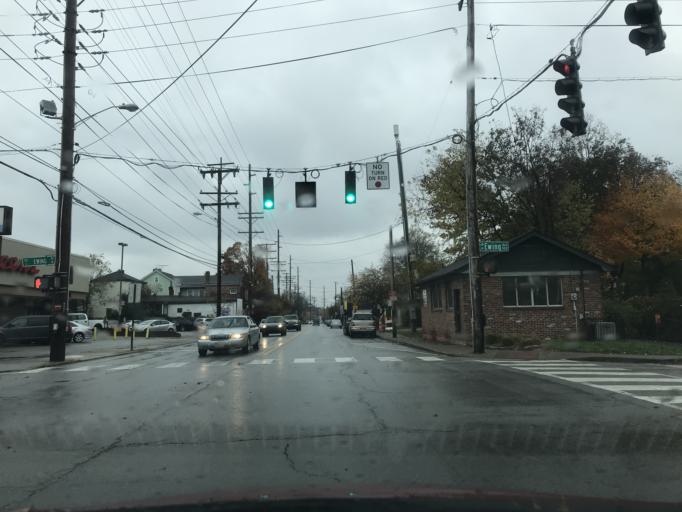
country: US
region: Kentucky
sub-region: Jefferson County
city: Indian Hills
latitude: 38.2538
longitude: -85.6998
